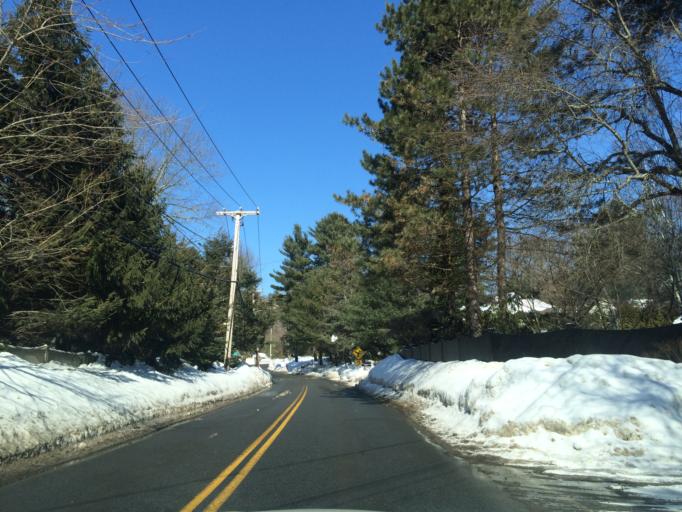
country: US
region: Massachusetts
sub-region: Norfolk County
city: Wellesley
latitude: 42.2801
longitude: -71.2879
